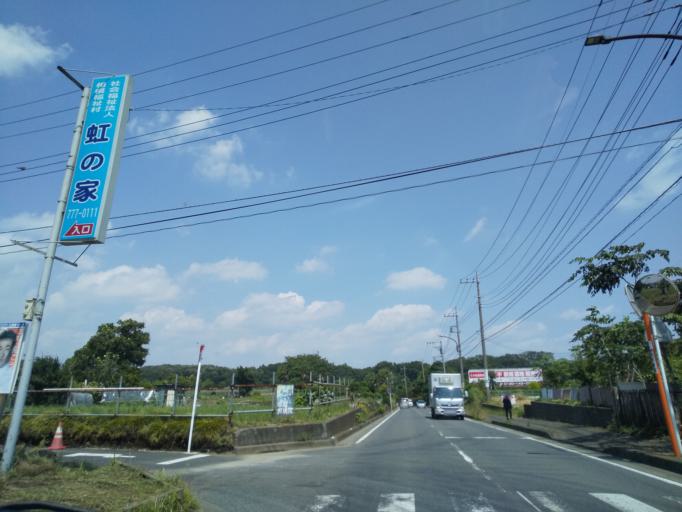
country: JP
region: Kanagawa
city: Zama
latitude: 35.5190
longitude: 139.3888
